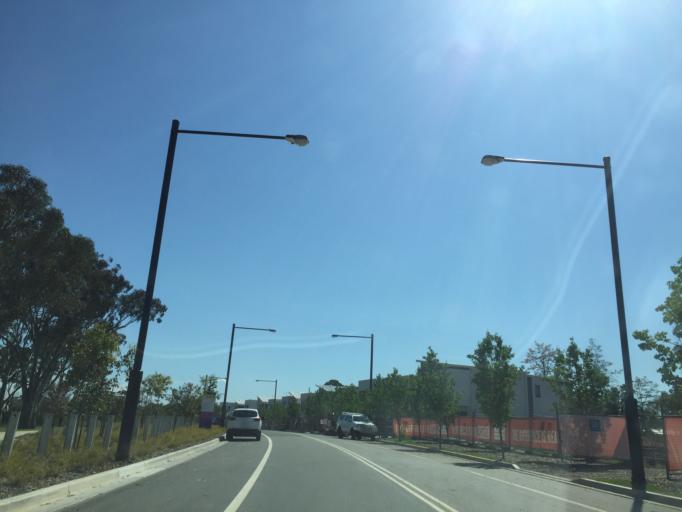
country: AU
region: New South Wales
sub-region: Blacktown
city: Blacktown
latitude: -33.7618
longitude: 150.9019
